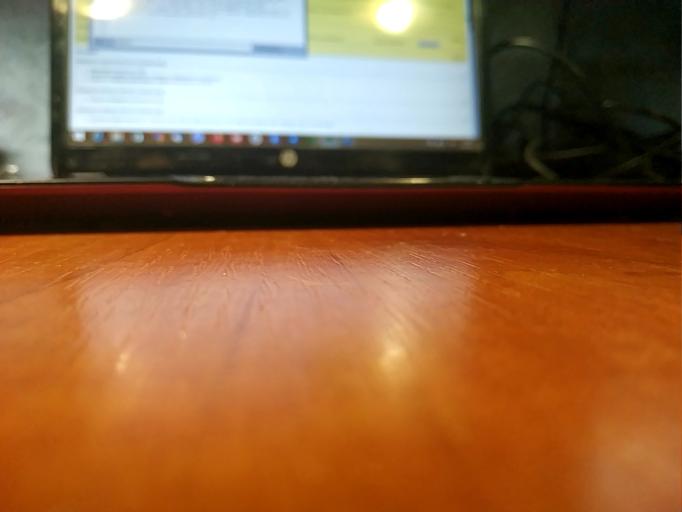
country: RU
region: Vologda
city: Ustyuzhna
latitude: 58.6660
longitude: 36.4249
